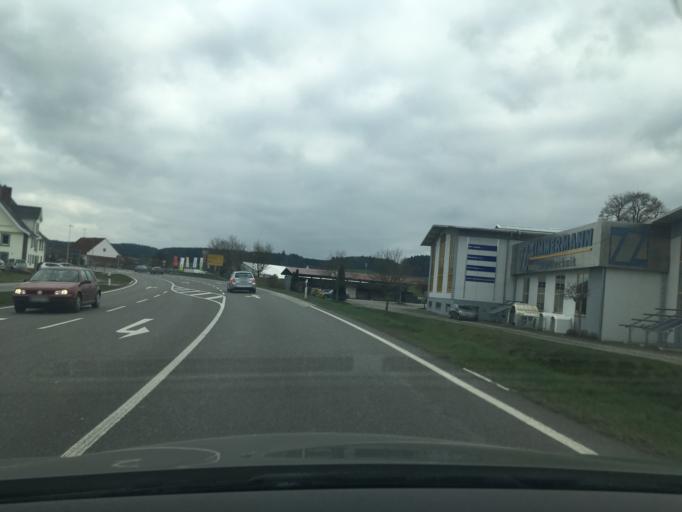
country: DE
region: Baden-Wuerttemberg
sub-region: Tuebingen Region
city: Eberhardzell
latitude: 47.9863
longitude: 9.7733
